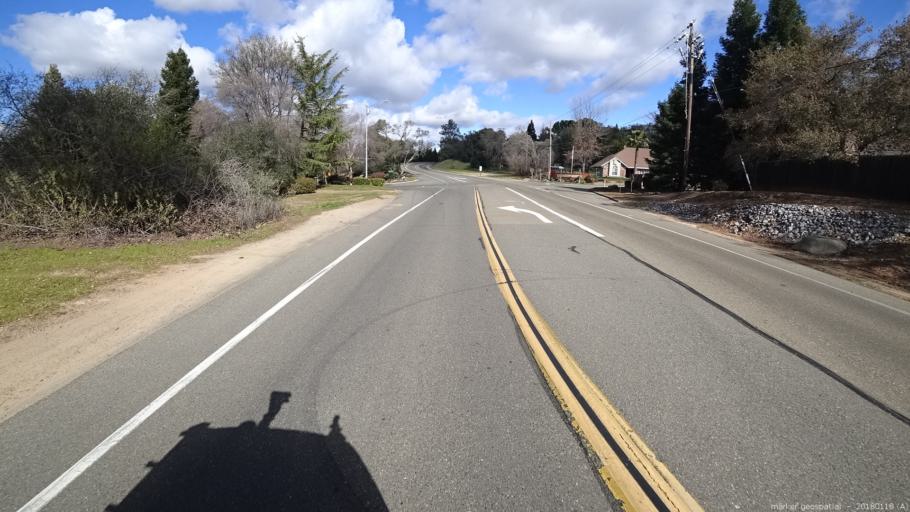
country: US
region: California
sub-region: Sacramento County
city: Folsom
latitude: 38.7150
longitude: -121.1886
